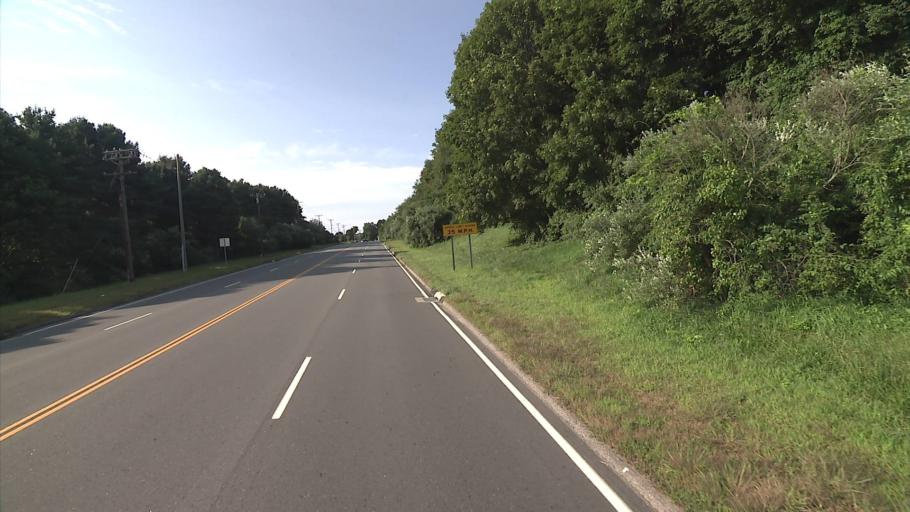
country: US
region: Connecticut
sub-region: New London County
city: Pawcatuck
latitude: 41.3919
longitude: -71.8453
